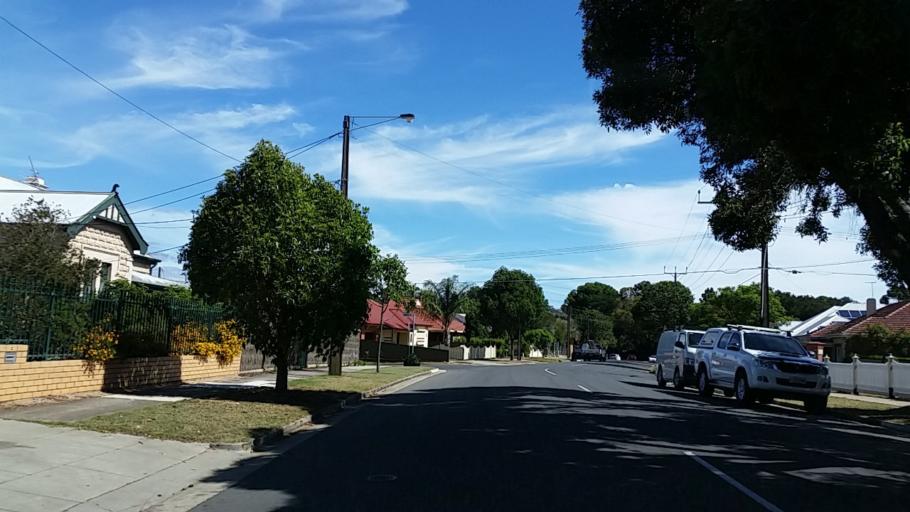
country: AU
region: South Australia
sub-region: Charles Sturt
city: Findon
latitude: -34.9247
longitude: 138.5322
